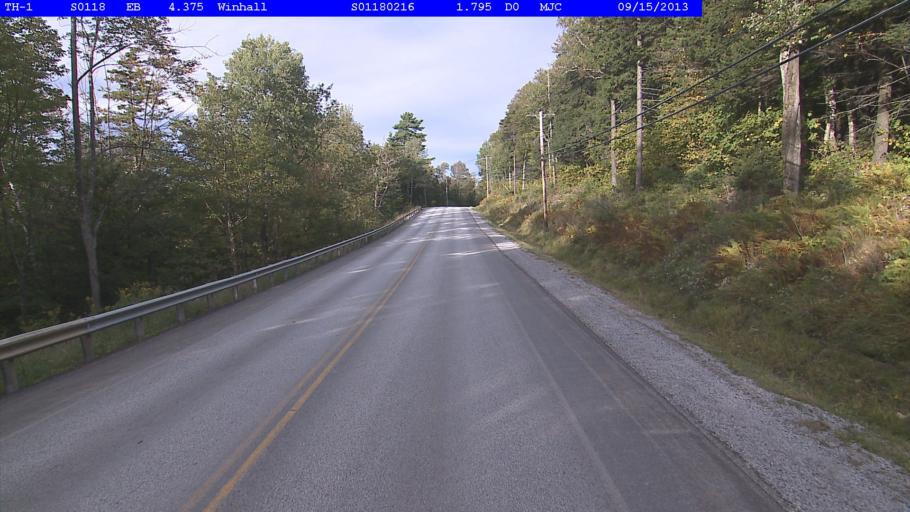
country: US
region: Vermont
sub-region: Bennington County
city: Manchester Center
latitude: 43.1338
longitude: -72.8975
